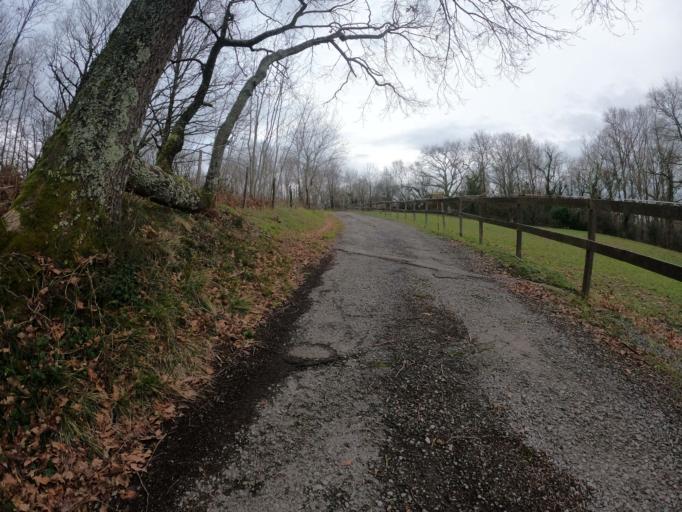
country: FR
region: Aquitaine
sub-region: Departement des Pyrenees-Atlantiques
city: Mazeres-Lezons
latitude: 43.2692
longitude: -0.3553
